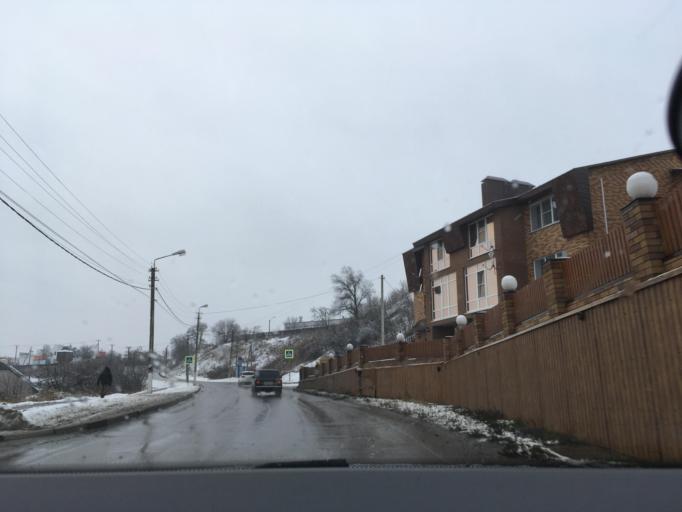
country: RU
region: Belgorod
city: Valuyki
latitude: 50.2117
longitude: 38.1070
